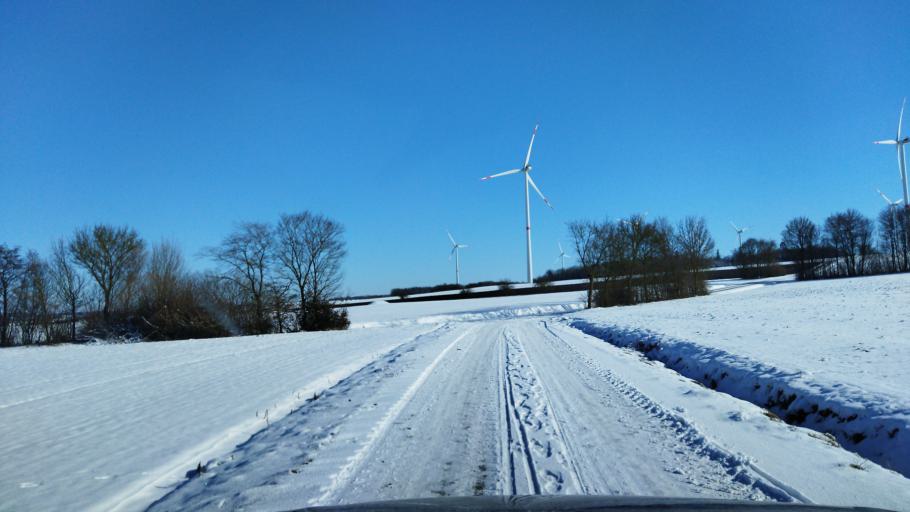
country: DE
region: Baden-Wuerttemberg
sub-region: Regierungsbezirk Stuttgart
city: Ilshofen
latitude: 49.1932
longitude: 9.9390
